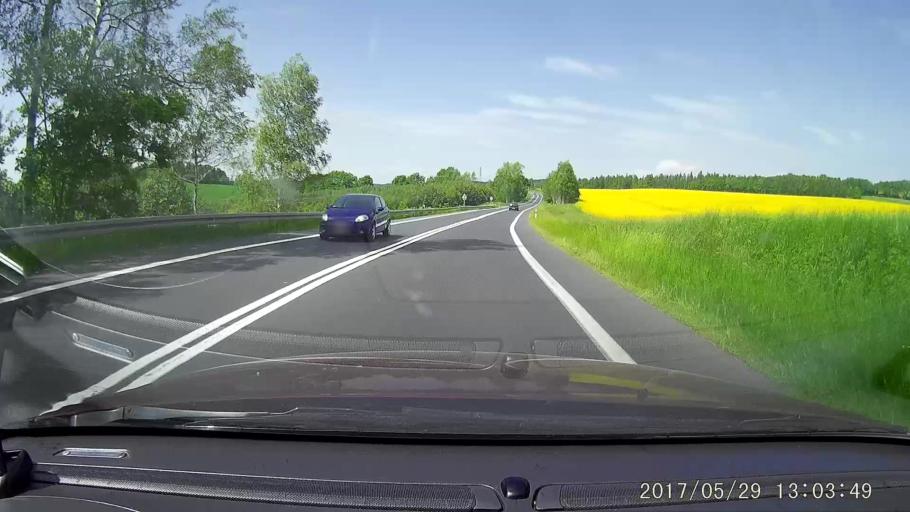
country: PL
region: Lower Silesian Voivodeship
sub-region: Powiat jeleniogorski
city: Stara Kamienica
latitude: 50.9256
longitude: 15.6078
